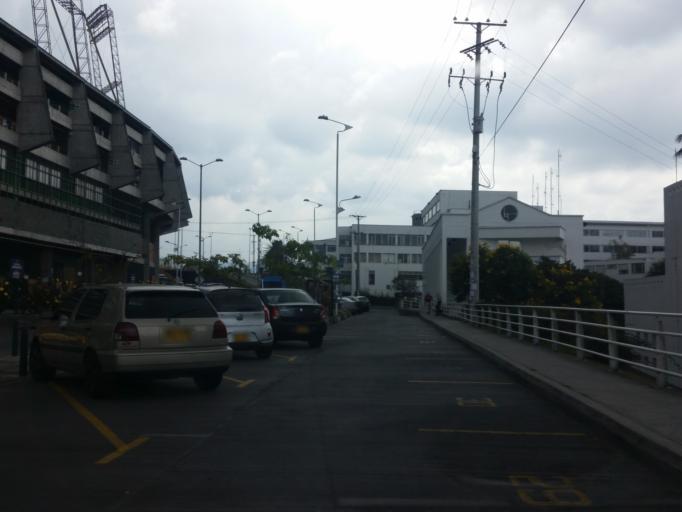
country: CO
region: Caldas
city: Villamaria
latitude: 5.0575
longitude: -75.4910
